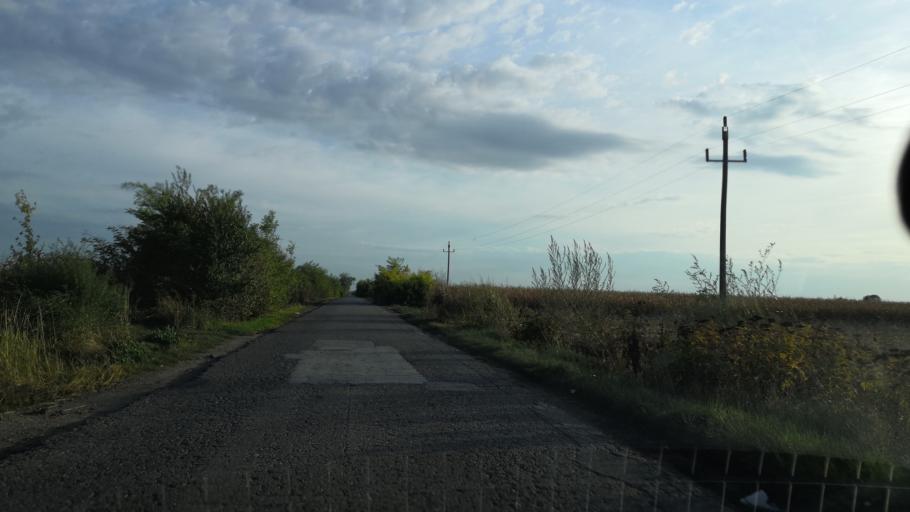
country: RS
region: Autonomna Pokrajina Vojvodina
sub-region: Sremski Okrug
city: Stara Pazova
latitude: 45.0218
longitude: 20.1701
